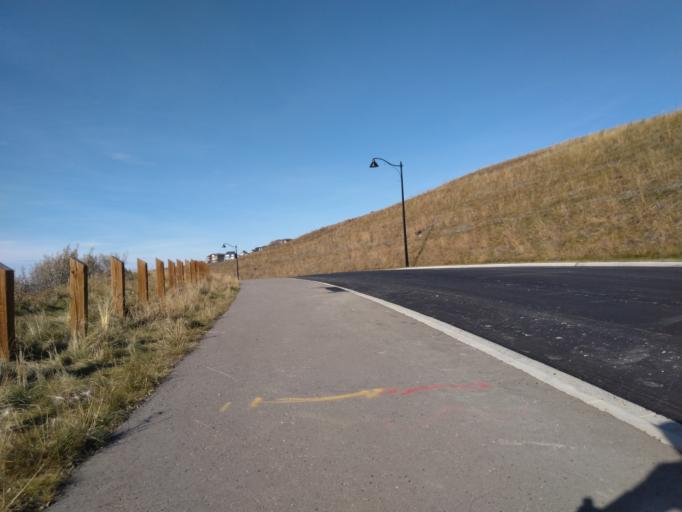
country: CA
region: Alberta
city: Calgary
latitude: 51.1768
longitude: -114.1265
